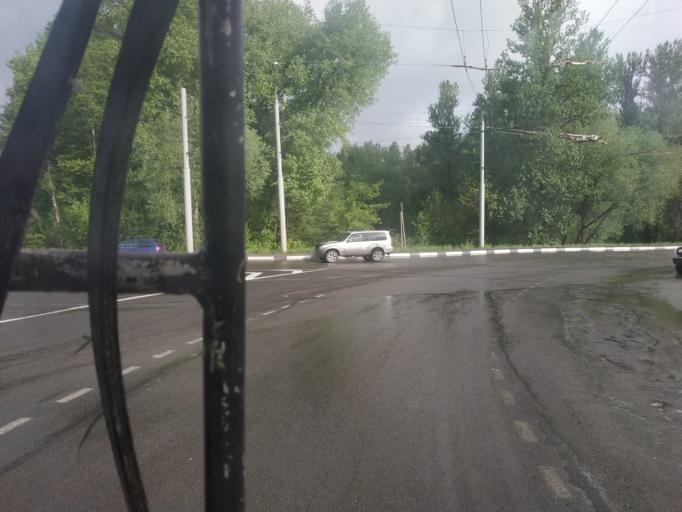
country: RU
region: Brjansk
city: Putevka
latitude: 53.2882
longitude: 34.3030
